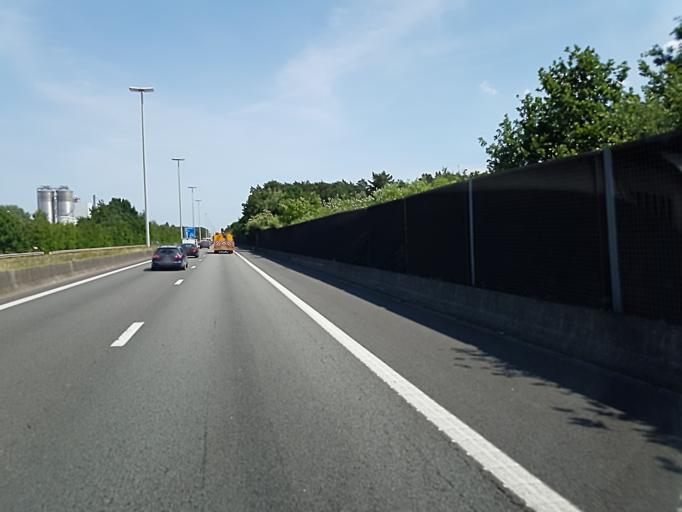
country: BE
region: Flanders
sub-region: Provincie Antwerpen
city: Laakdal
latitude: 51.1119
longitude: 5.0027
